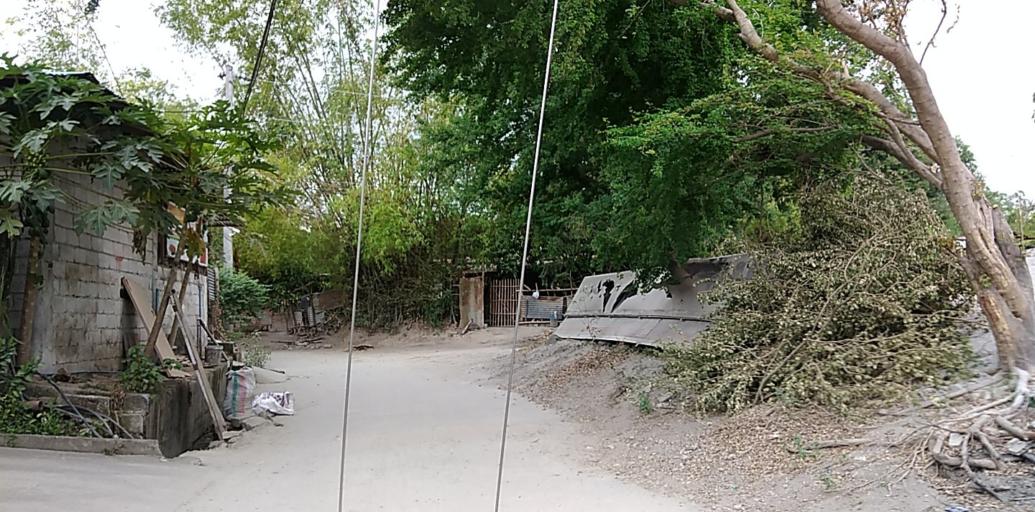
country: PH
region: Central Luzon
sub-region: Province of Pampanga
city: Pulung Santol
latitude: 15.0459
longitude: 120.5614
